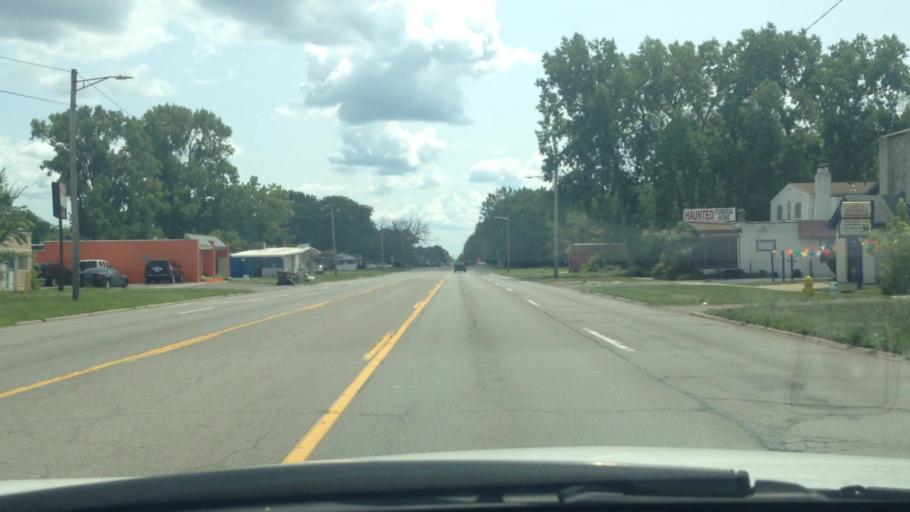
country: US
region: Michigan
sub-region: Wayne County
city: Inkster
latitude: 42.2812
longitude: -83.3095
